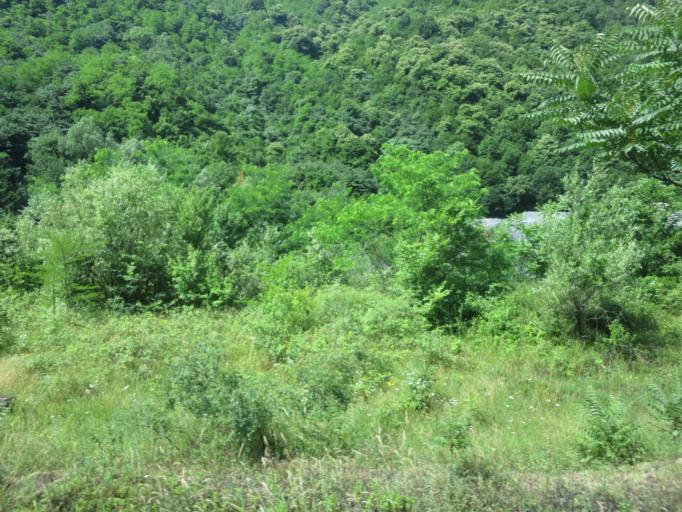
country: GE
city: Shorapani
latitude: 42.0821
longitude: 43.1422
